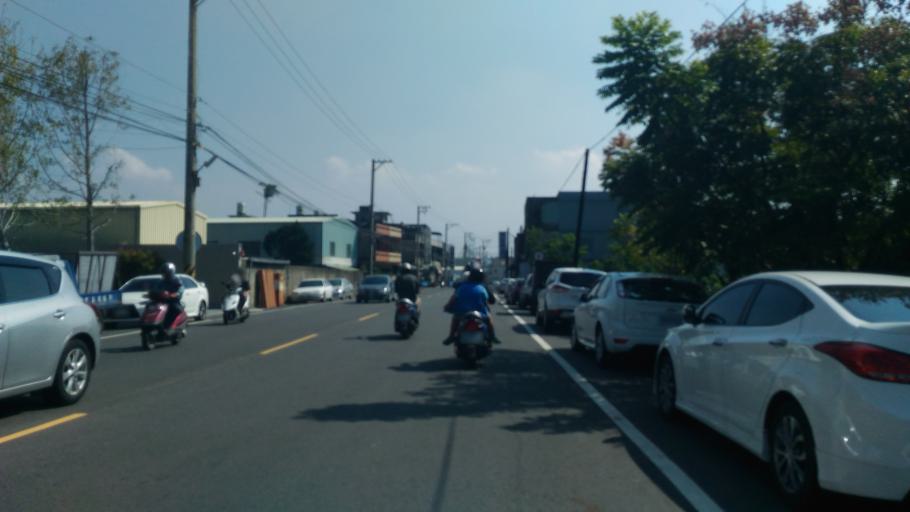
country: TW
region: Taiwan
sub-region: Hsinchu
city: Hsinchu
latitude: 24.8343
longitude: 120.9466
